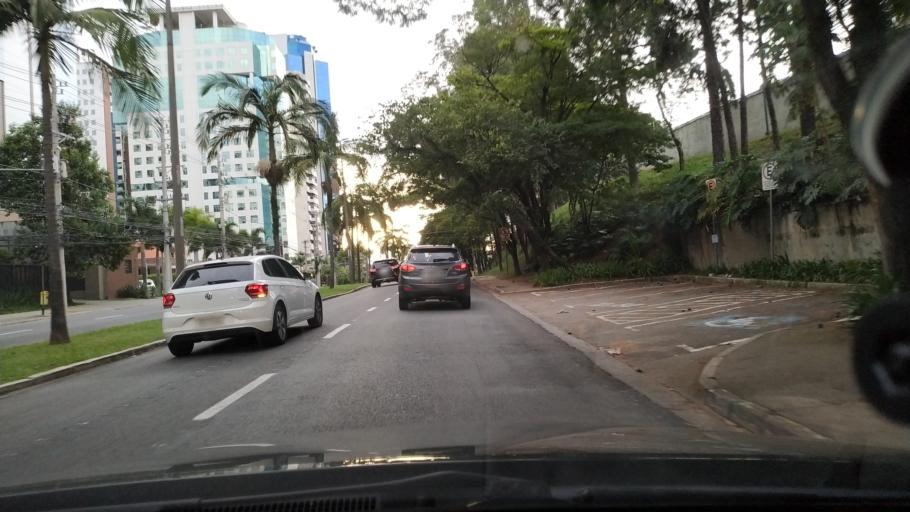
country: BR
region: Sao Paulo
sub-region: Barueri
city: Barueri
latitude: -23.4925
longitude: -46.8504
